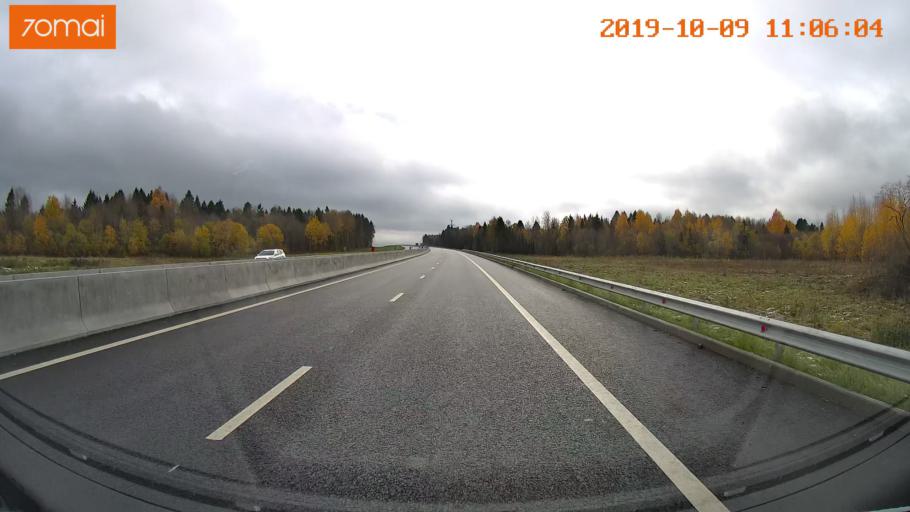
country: RU
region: Vologda
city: Molochnoye
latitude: 59.1915
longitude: 39.7583
